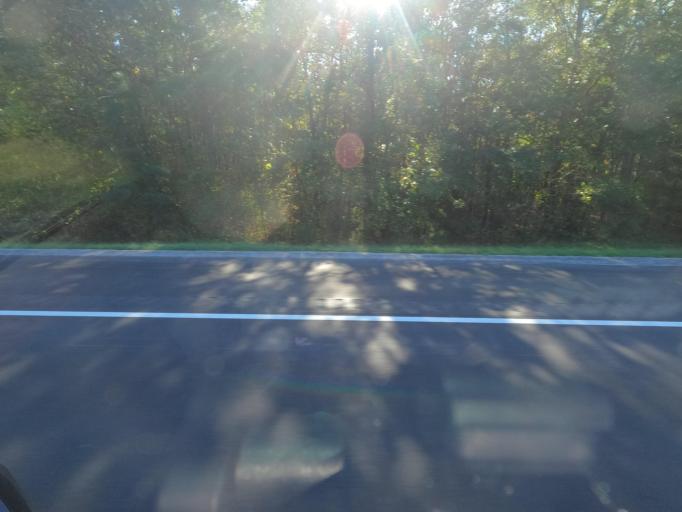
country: US
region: Tennessee
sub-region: Coffee County
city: Manchester
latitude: 35.4221
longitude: -86.0214
